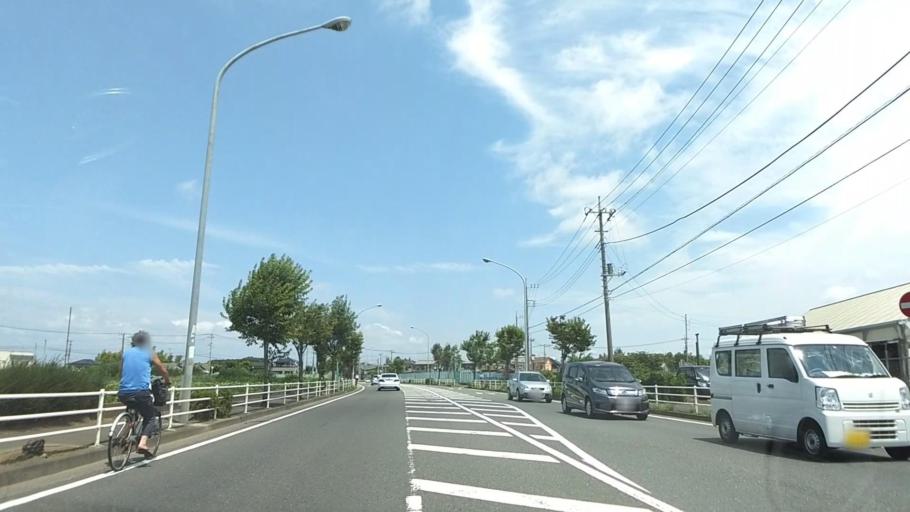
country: JP
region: Kanagawa
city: Minami-rinkan
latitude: 35.4485
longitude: 139.4840
